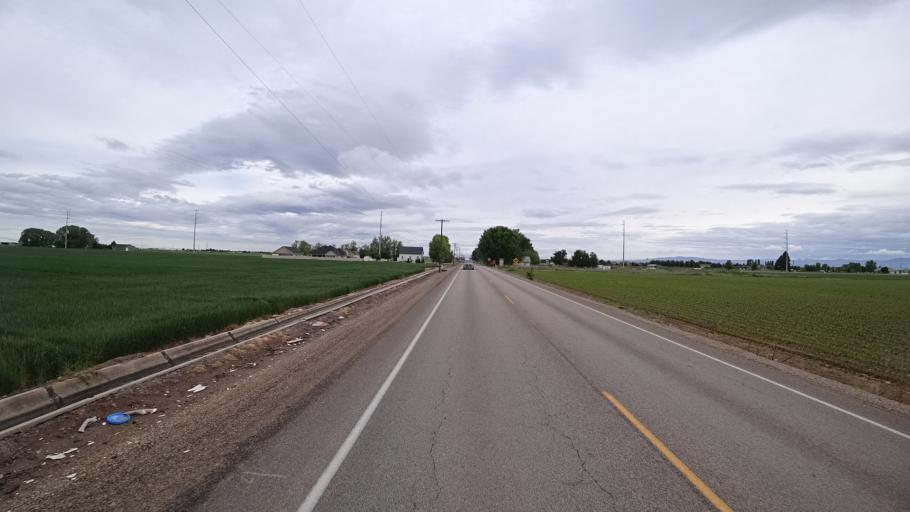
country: US
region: Idaho
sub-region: Ada County
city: Star
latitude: 43.6464
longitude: -116.4936
